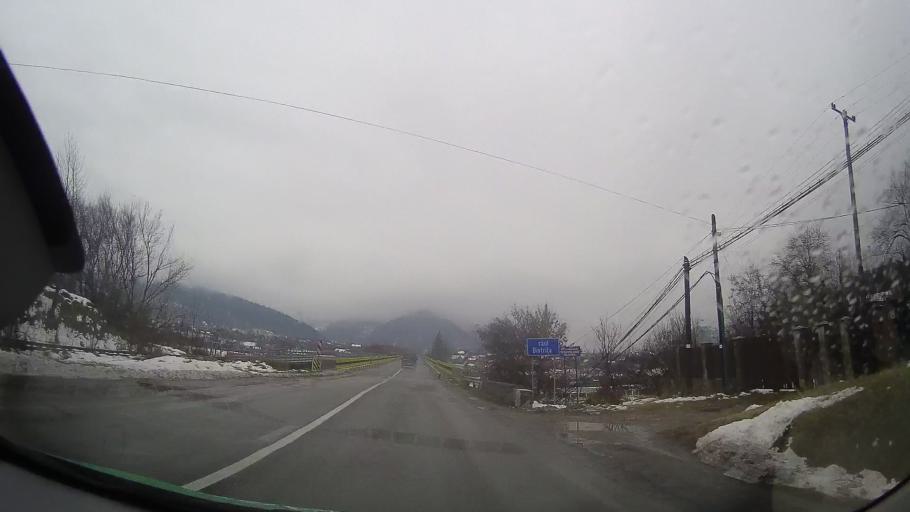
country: RO
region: Neamt
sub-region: Comuna Alexandru Cel Bun
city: Vadurele
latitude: 46.9395
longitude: 26.2654
